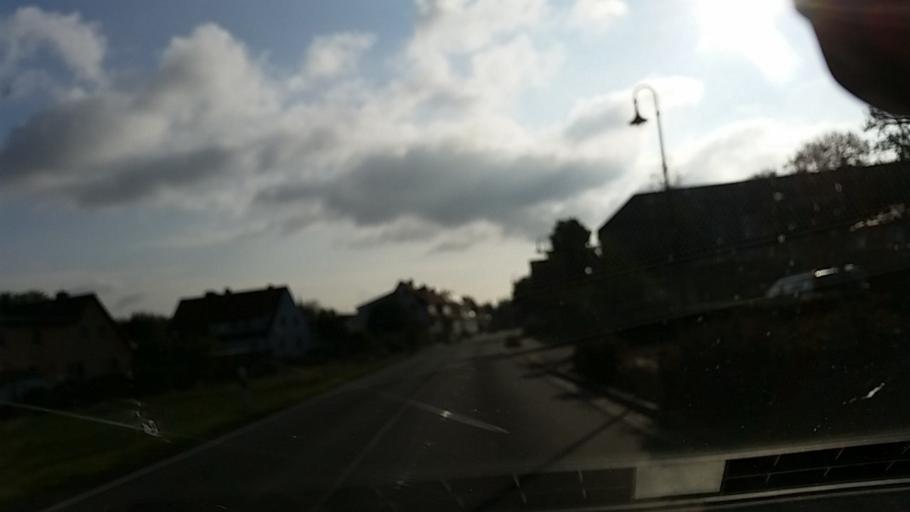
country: DE
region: Thuringia
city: Nohra
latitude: 51.4334
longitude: 10.6951
